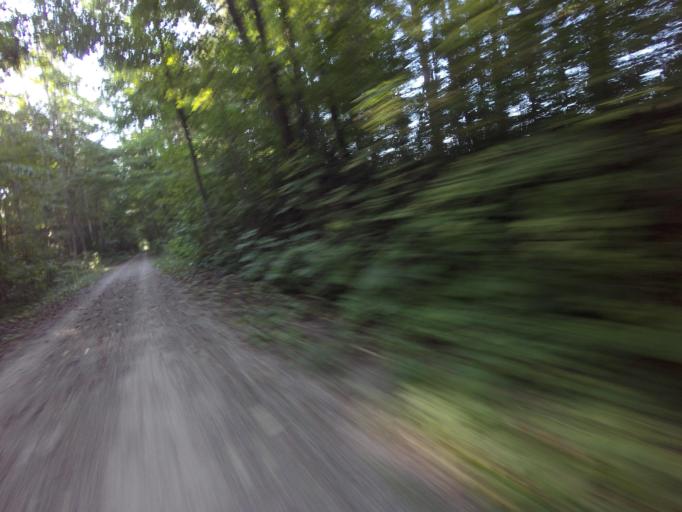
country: CA
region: Ontario
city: Goderich
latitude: 43.7472
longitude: -81.6415
